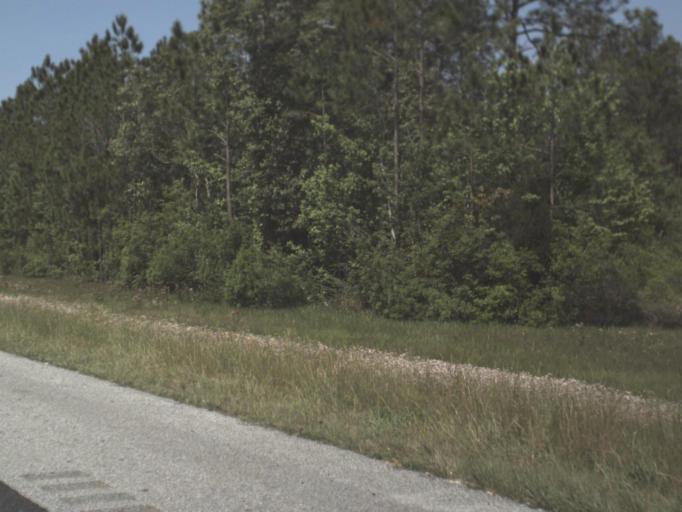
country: US
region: Florida
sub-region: Santa Rosa County
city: Bagdad
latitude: 30.5762
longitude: -87.0236
